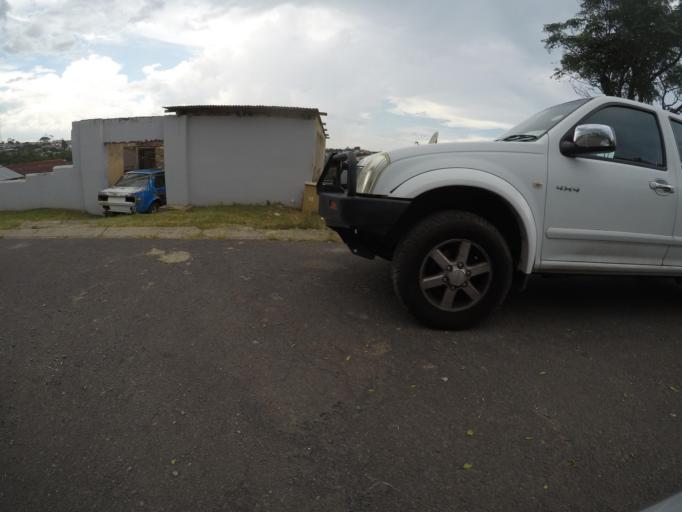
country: ZA
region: Eastern Cape
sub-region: Buffalo City Metropolitan Municipality
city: East London
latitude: -33.0202
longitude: 27.8698
